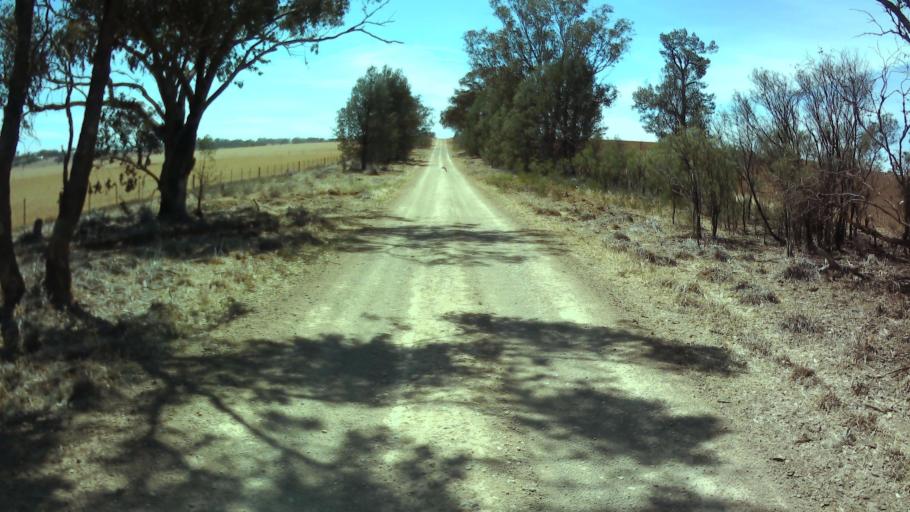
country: AU
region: New South Wales
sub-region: Weddin
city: Grenfell
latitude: -33.9437
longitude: 148.1490
